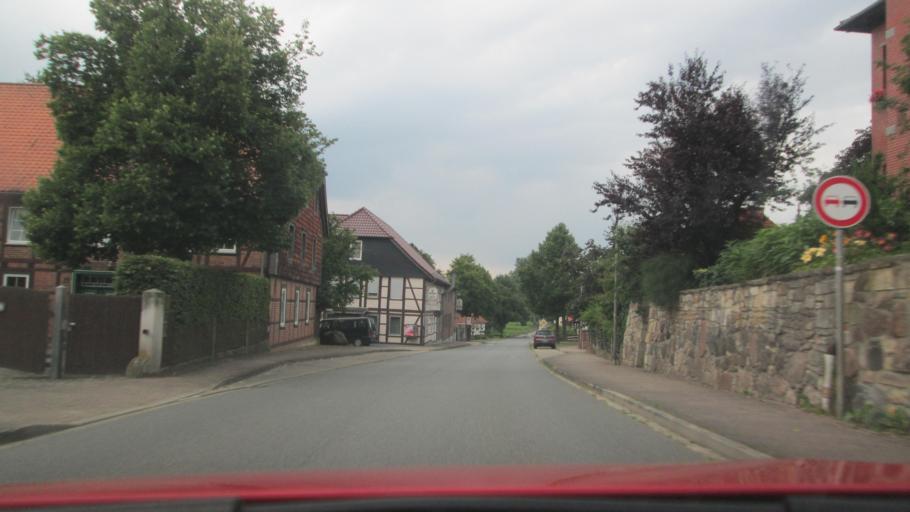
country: DE
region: Lower Saxony
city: Wolfsburg
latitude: 52.3596
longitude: 10.7447
